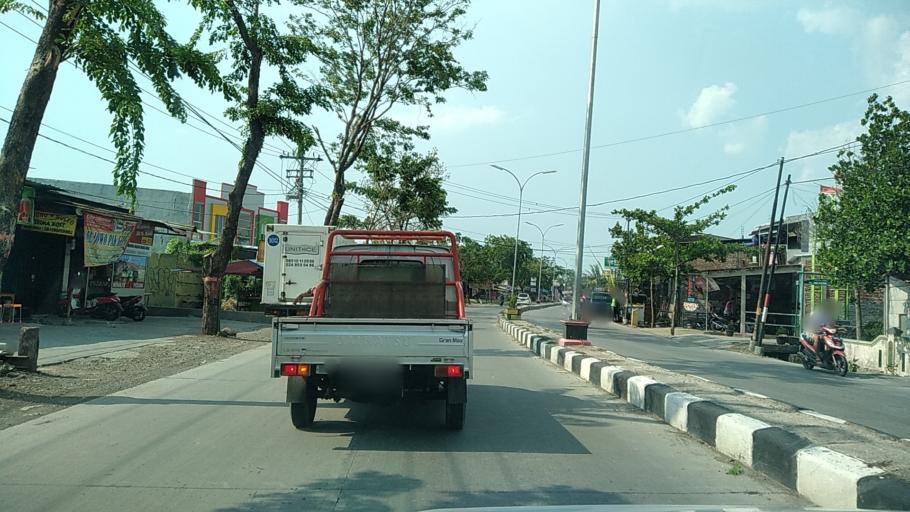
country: ID
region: Central Java
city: Semarang
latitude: -6.9637
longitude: 110.4787
